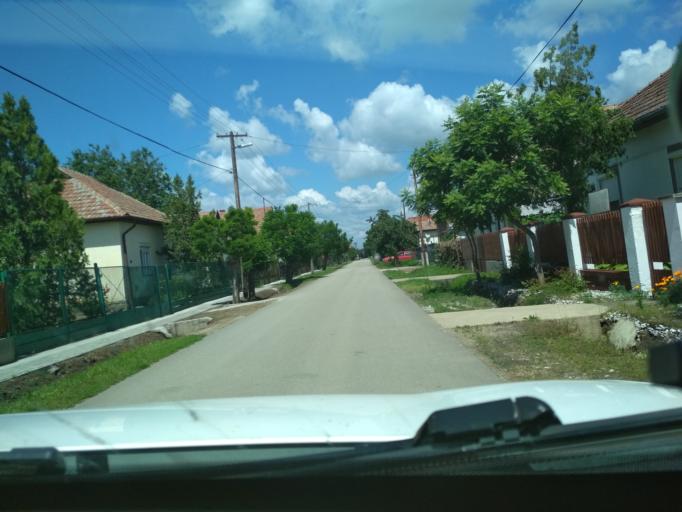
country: HU
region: Jasz-Nagykun-Szolnok
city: Abadszalok
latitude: 47.4803
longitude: 20.5972
